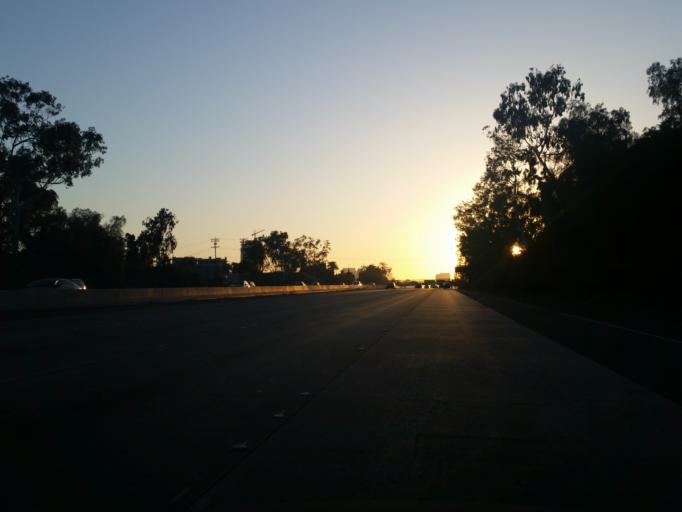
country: US
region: California
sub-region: San Diego County
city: San Diego
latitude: 32.7134
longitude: -117.1347
